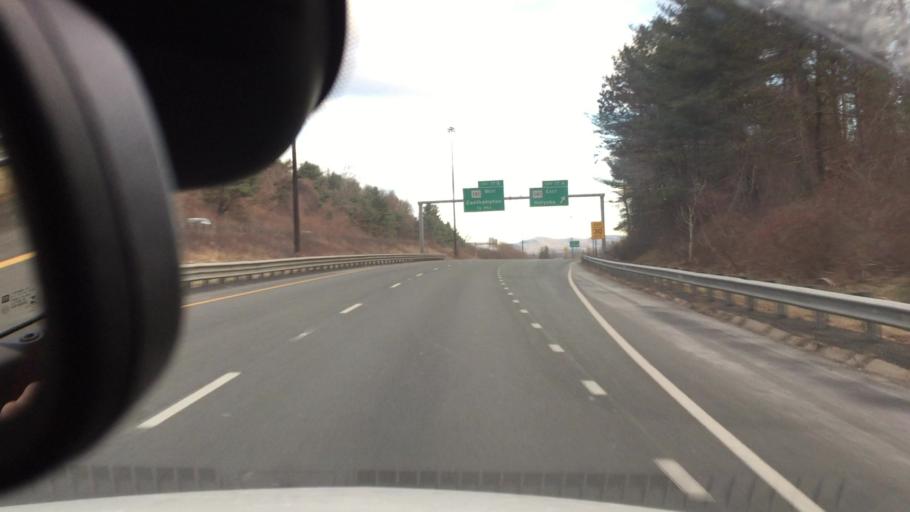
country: US
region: Massachusetts
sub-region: Hampden County
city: Holyoke
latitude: 42.2070
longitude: -72.6376
